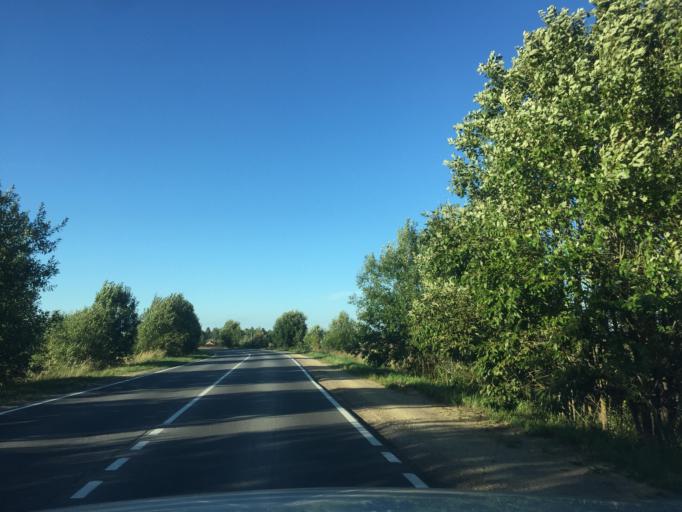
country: RU
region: Leningrad
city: Siverskiy
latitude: 59.3325
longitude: 30.0303
